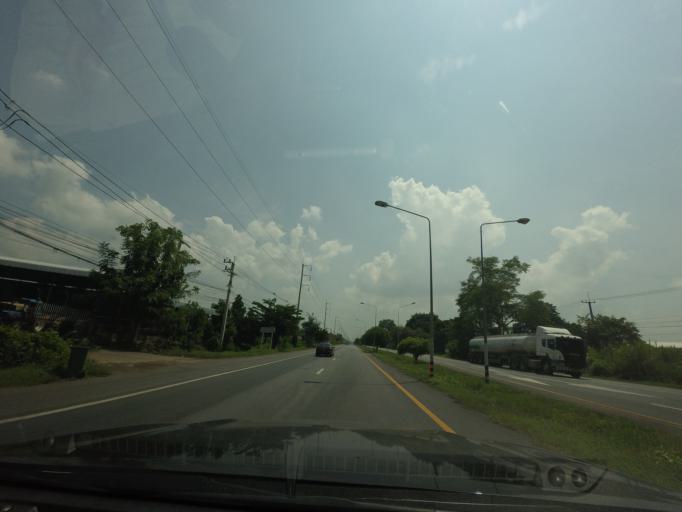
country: TH
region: Uttaradit
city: Uttaradit
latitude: 17.5816
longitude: 100.1423
